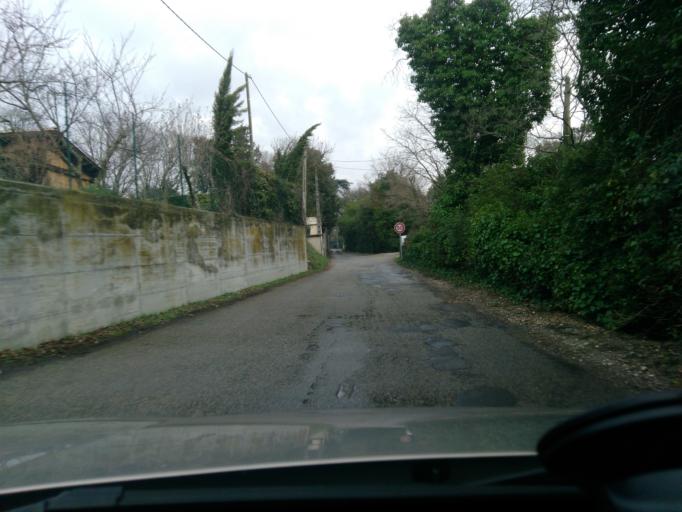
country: FR
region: Rhone-Alpes
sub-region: Departement de la Drome
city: Montelimar
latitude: 44.5549
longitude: 4.7664
